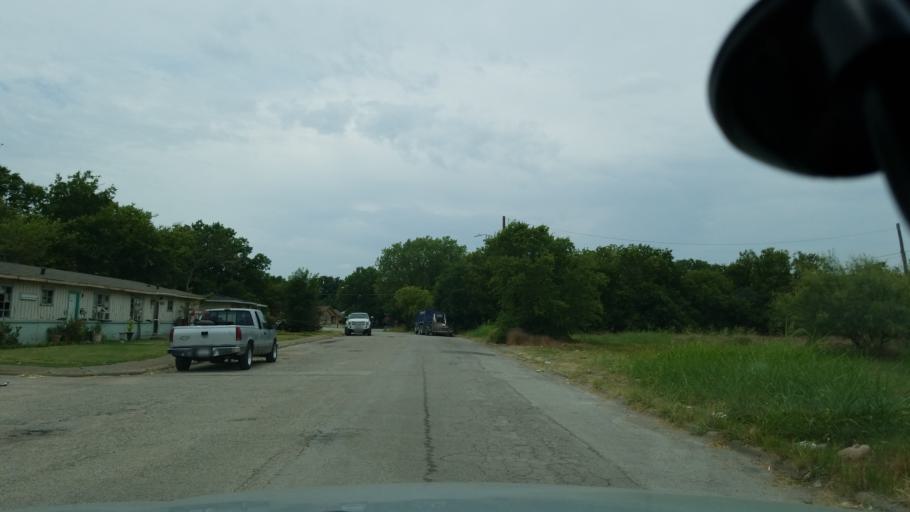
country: US
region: Texas
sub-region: Dallas County
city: Grand Prairie
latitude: 32.7377
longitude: -96.9862
